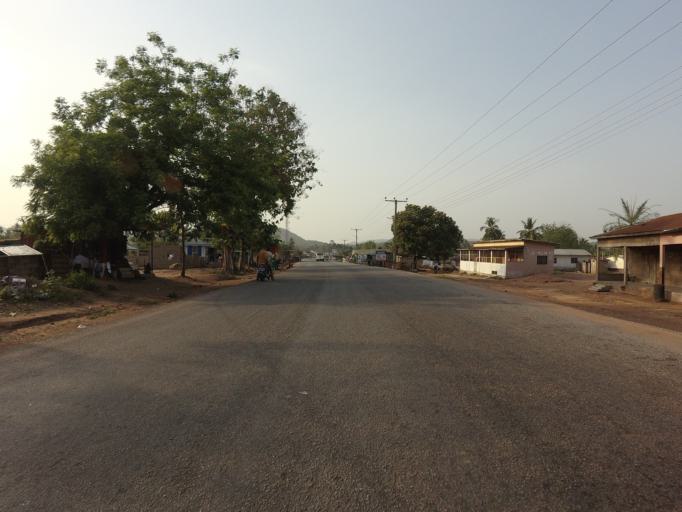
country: GH
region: Volta
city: Ho
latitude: 6.4057
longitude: 0.1753
